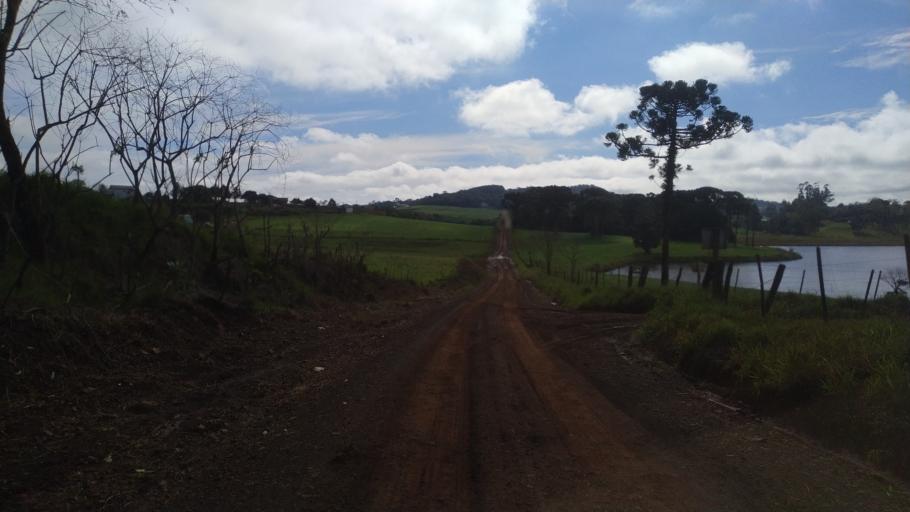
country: BR
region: Santa Catarina
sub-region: Chapeco
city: Chapeco
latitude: -27.1525
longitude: -52.5952
